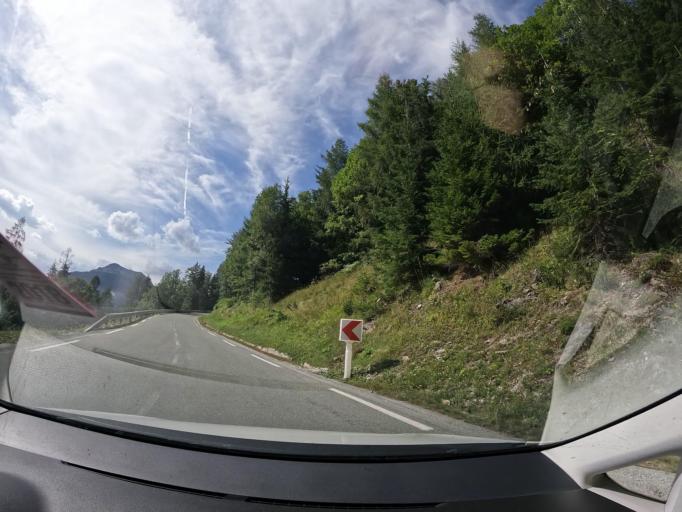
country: AT
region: Carinthia
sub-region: Politischer Bezirk Sankt Veit an der Glan
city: Liebenfels
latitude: 46.7209
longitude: 14.2486
